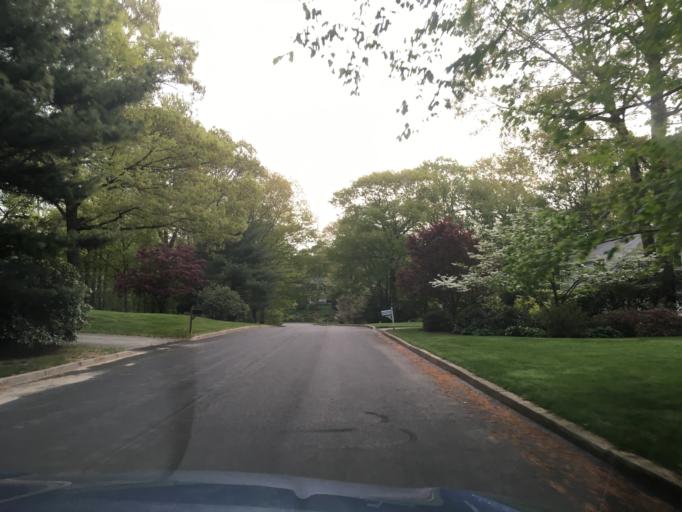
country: US
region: Rhode Island
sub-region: Kent County
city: West Warwick
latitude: 41.6596
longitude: -71.5158
